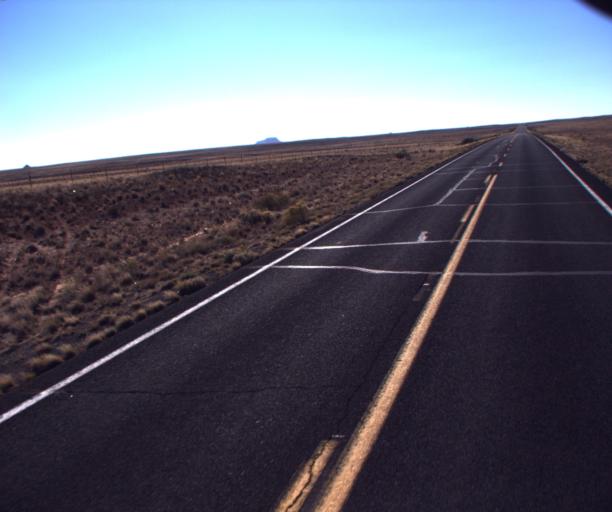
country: US
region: Arizona
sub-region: Navajo County
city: First Mesa
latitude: 35.6625
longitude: -110.4937
